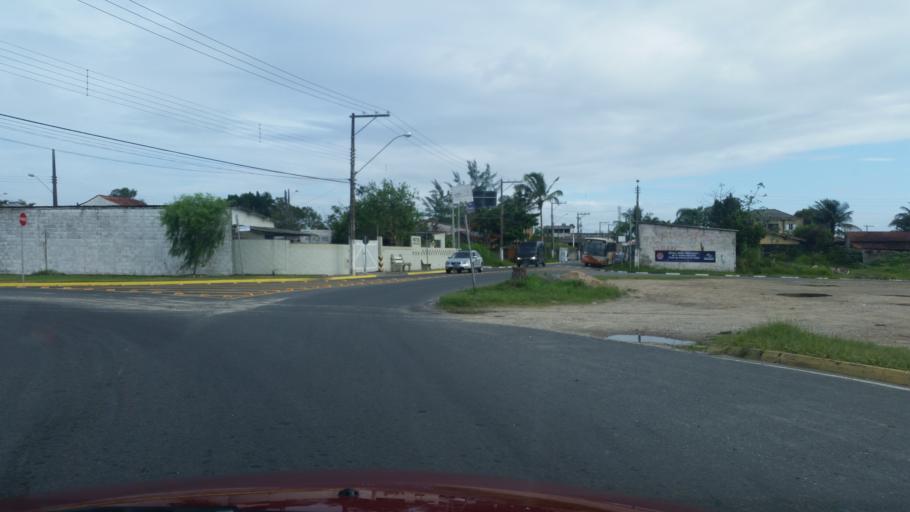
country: BR
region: Sao Paulo
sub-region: Iguape
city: Iguape
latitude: -24.7391
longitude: -47.5551
